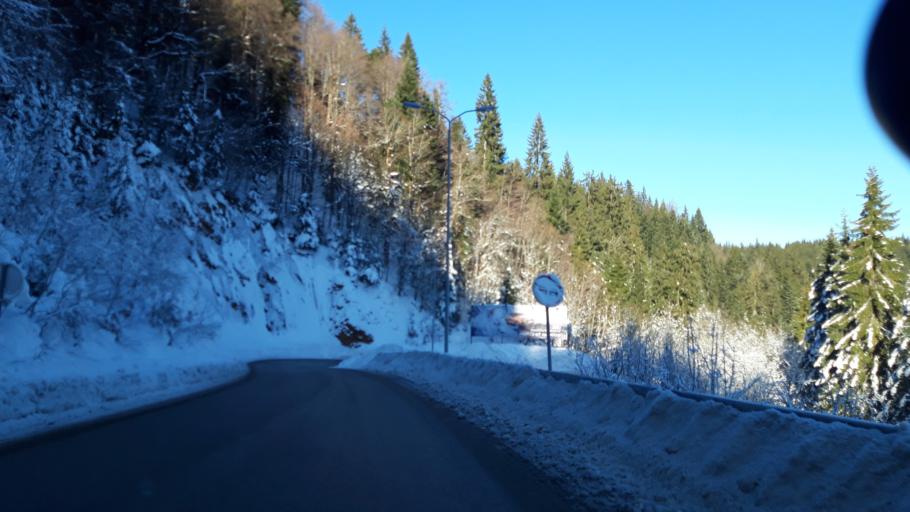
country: BA
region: Republika Srpska
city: Koran
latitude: 43.7432
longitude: 18.5658
